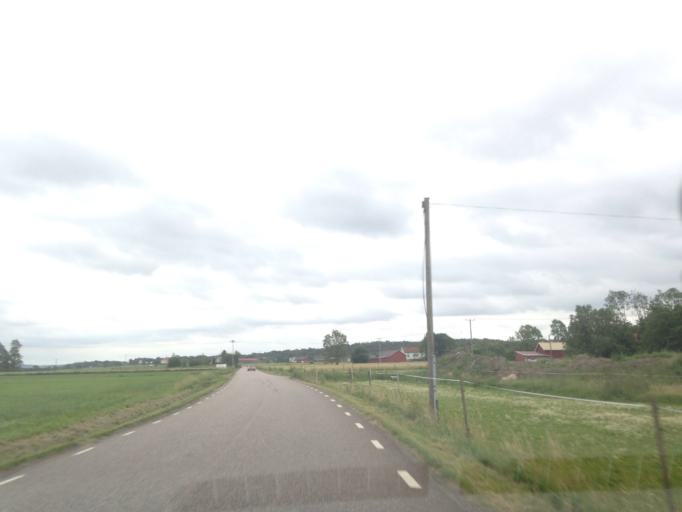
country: SE
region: Vaestra Goetaland
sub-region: Kungalvs Kommun
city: Kode
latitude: 57.8263
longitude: 11.8179
